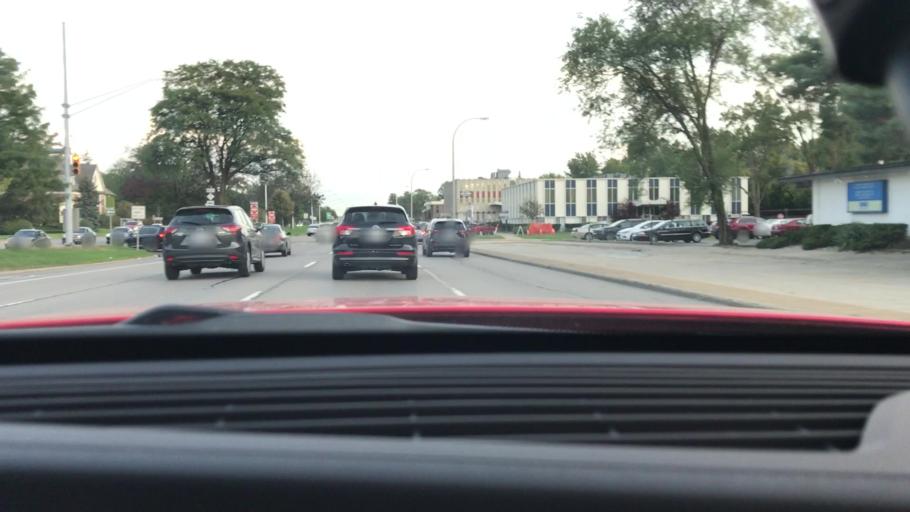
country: US
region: Michigan
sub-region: Oakland County
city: Huntington Woods
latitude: 42.4891
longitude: -83.1586
